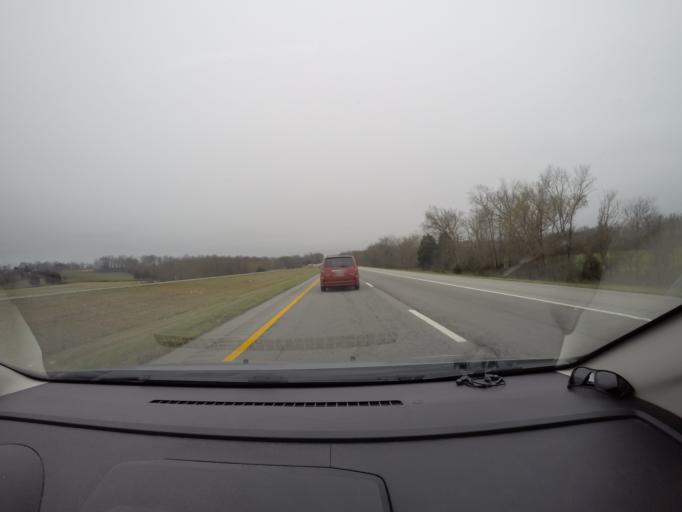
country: US
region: Tennessee
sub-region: Coffee County
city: Manchester
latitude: 35.3739
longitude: -85.9728
